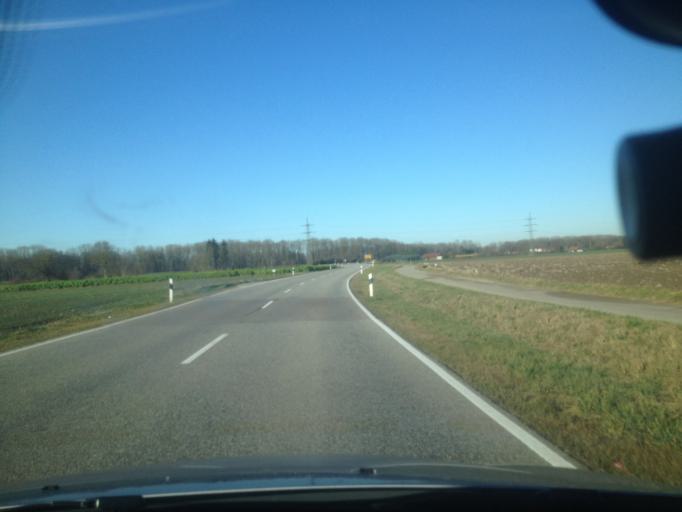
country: DE
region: Bavaria
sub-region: Upper Bavaria
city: Moosburg
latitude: 48.4559
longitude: 11.9563
